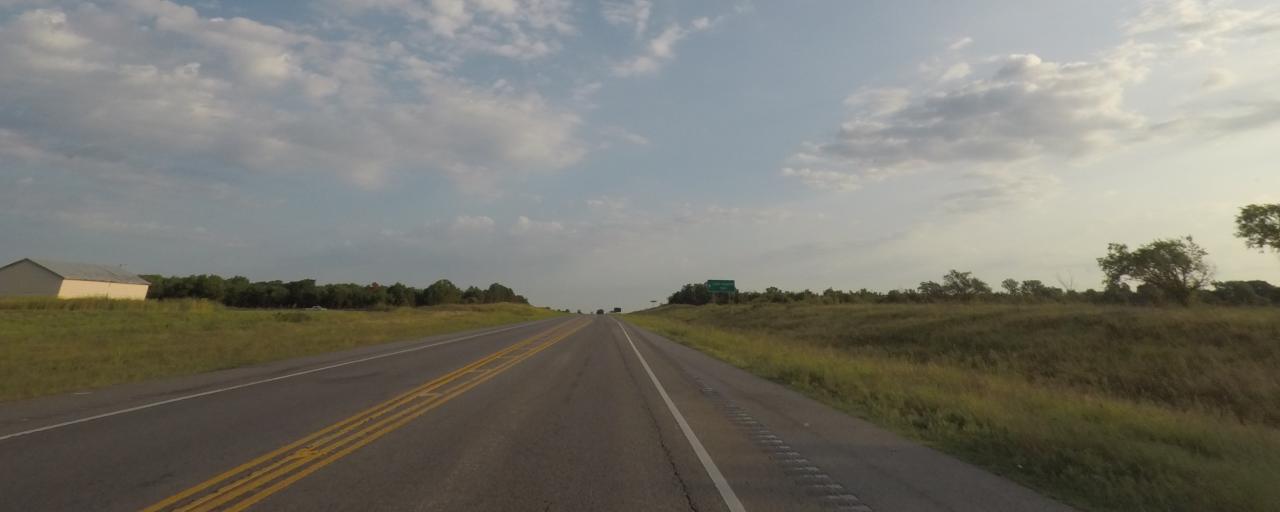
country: US
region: Oklahoma
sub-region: Stephens County
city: Meridian
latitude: 34.4471
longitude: -97.9741
